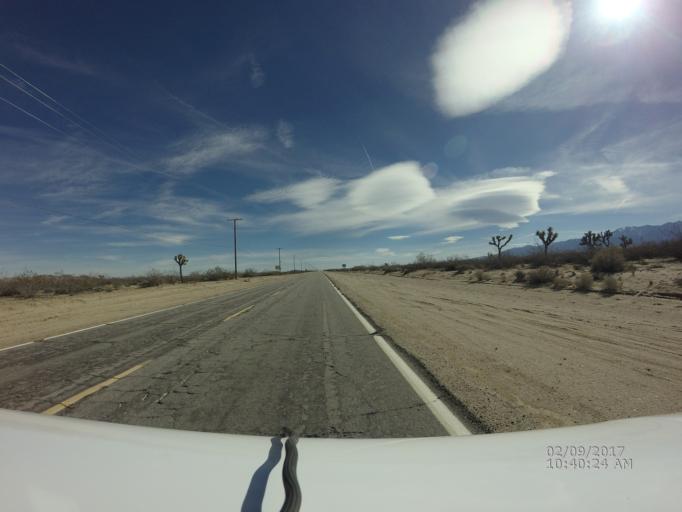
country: US
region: California
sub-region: Los Angeles County
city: Littlerock
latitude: 34.5428
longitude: -117.9155
